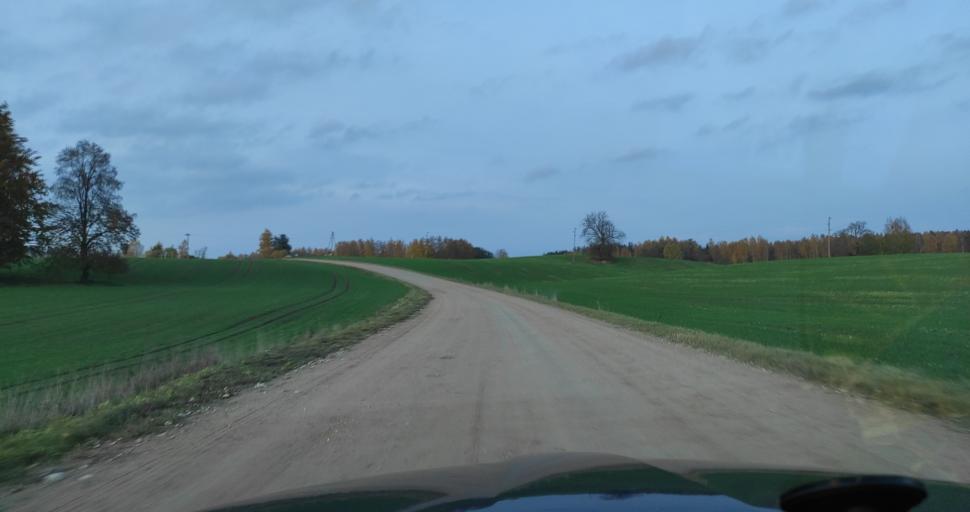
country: LV
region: Aizpute
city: Aizpute
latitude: 56.6573
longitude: 21.7957
